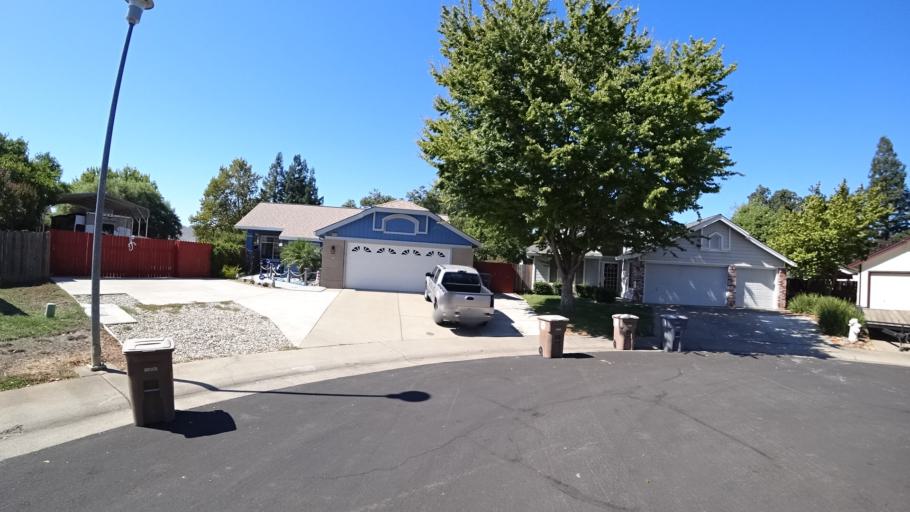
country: US
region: California
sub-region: Sacramento County
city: Laguna
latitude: 38.4345
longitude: -121.4346
